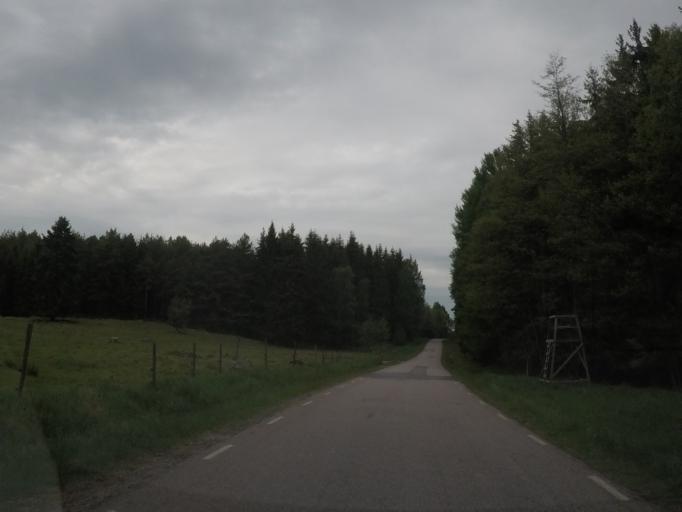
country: SE
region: Soedermanland
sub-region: Nykopings Kommun
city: Stigtomta
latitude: 58.9271
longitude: 16.8846
